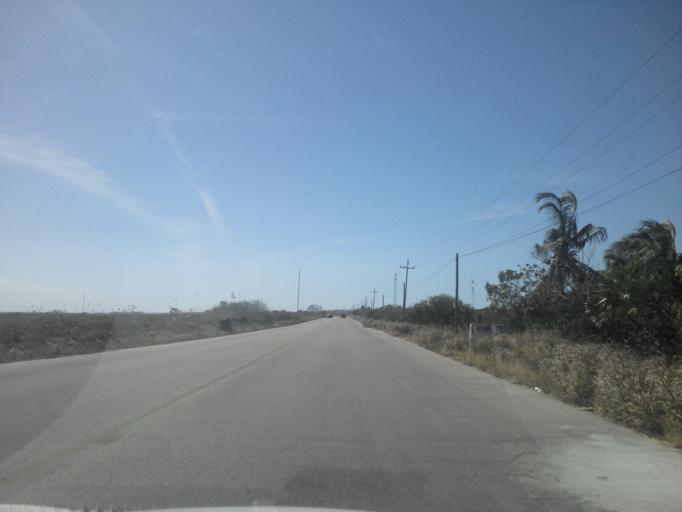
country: MX
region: Yucatan
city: Telchac Puerto
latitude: 21.3289
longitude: -89.3857
